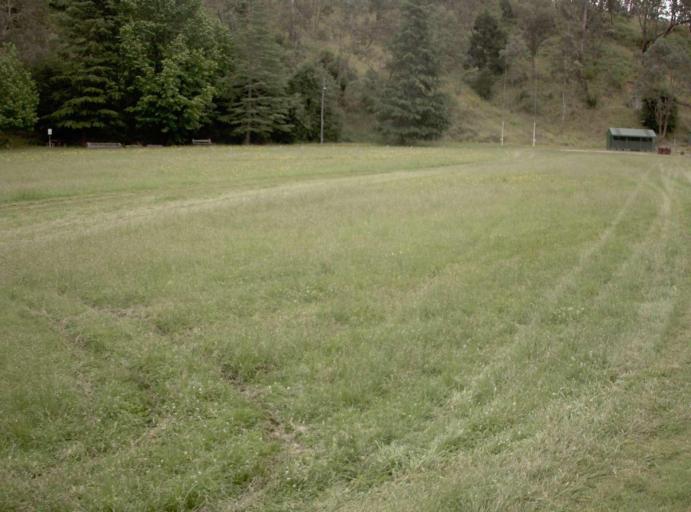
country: AU
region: Victoria
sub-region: East Gippsland
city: Bairnsdale
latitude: -37.4567
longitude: 147.2510
